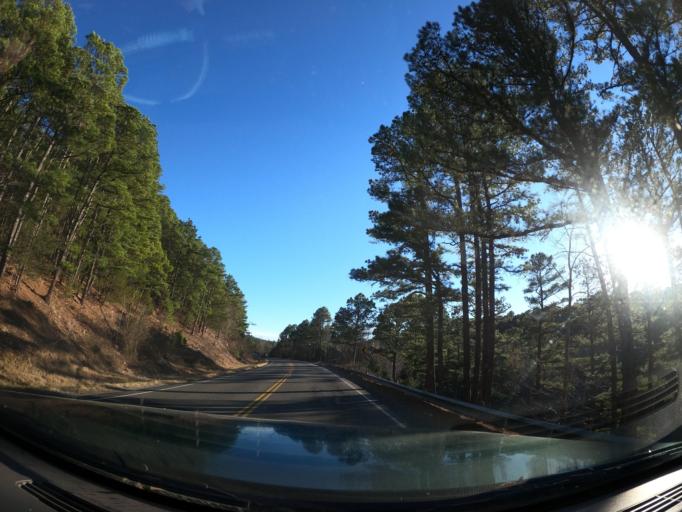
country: US
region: Oklahoma
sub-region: Latimer County
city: Wilburton
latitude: 34.9771
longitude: -95.3594
